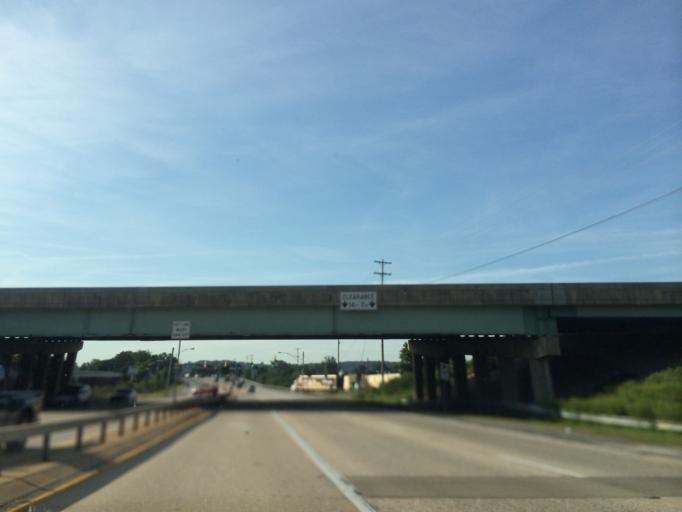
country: US
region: Pennsylvania
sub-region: York County
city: Yorklyn
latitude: 39.9869
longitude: -76.6679
